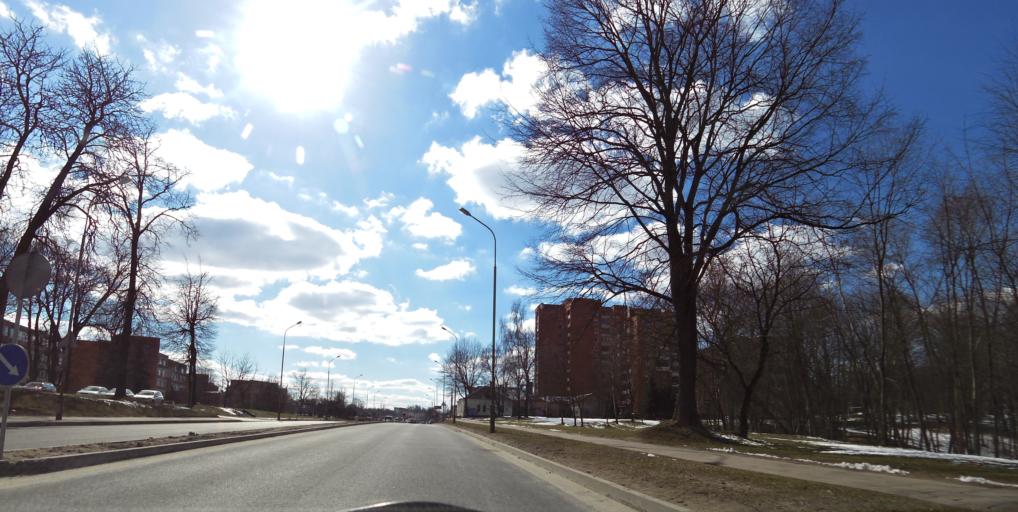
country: LT
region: Vilnius County
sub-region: Vilnius
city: Fabijoniskes
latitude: 54.7467
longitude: 25.2786
